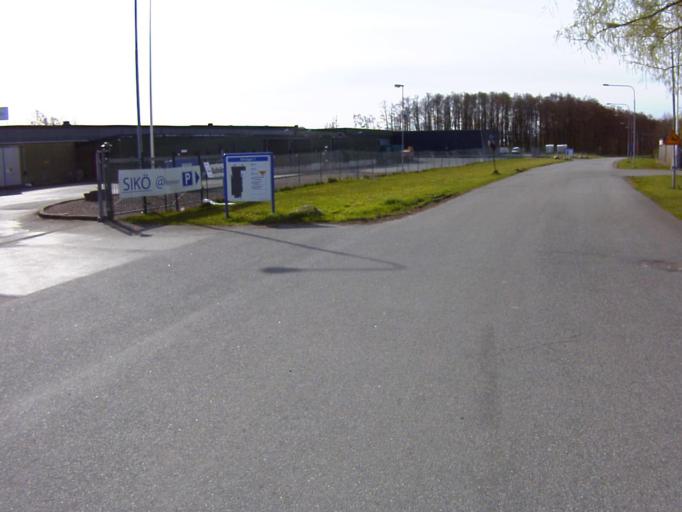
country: SE
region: Skane
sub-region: Kristianstads Kommun
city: Kristianstad
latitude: 56.0128
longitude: 14.1556
